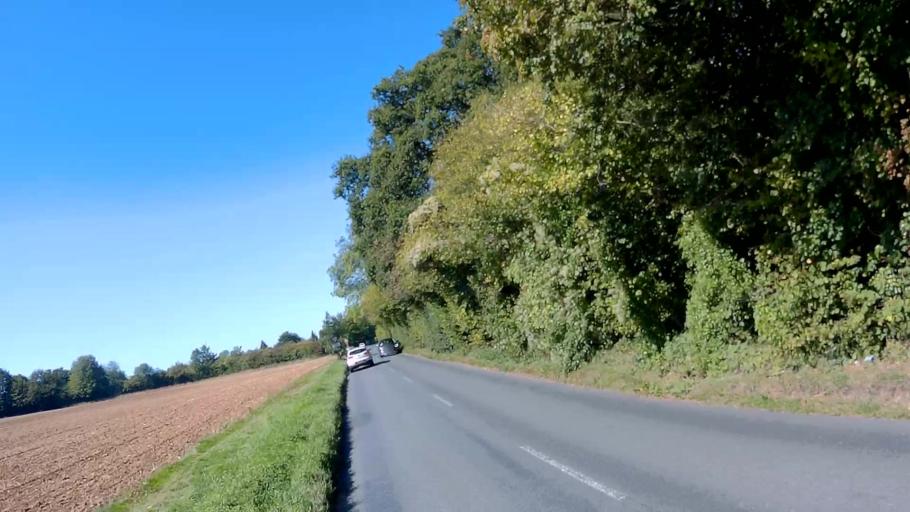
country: GB
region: England
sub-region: Hampshire
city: Basingstoke
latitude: 51.2544
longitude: -1.1674
